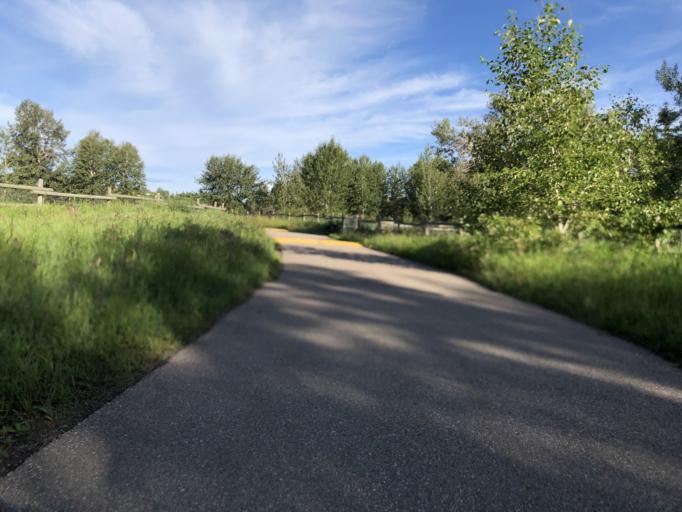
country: CA
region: Alberta
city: Calgary
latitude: 50.9694
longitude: -114.0278
